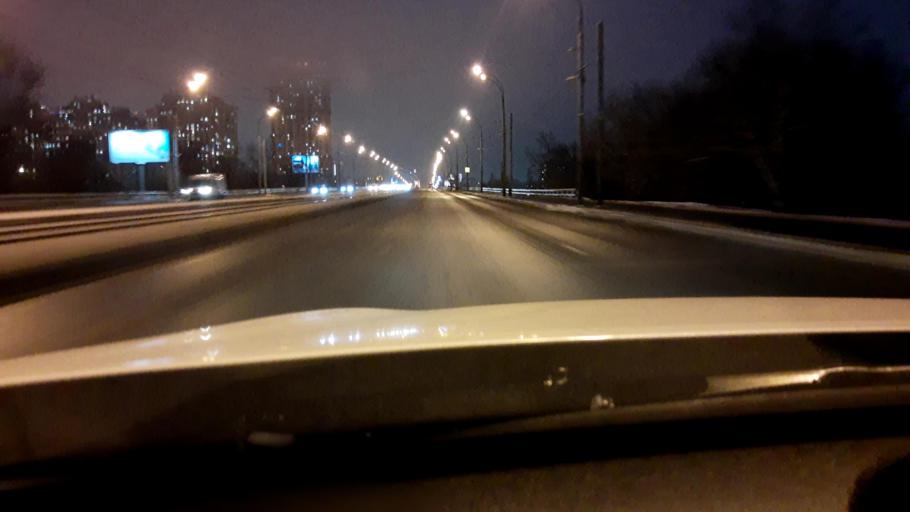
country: RU
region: Moscow
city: Shchukino
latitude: 55.8045
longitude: 37.4372
